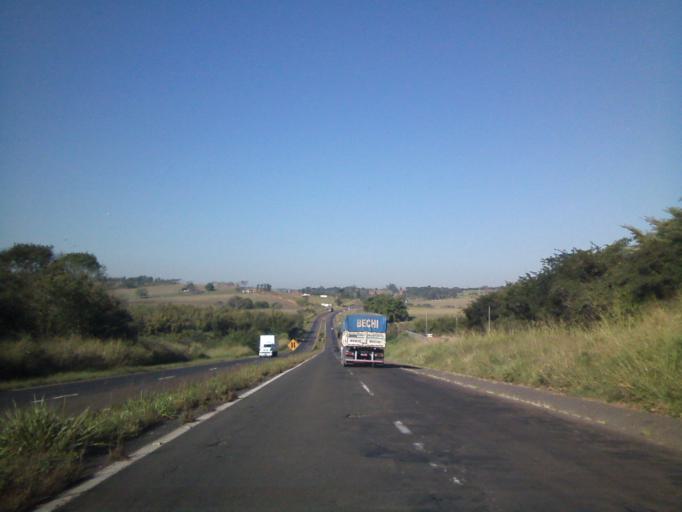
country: BR
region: Sao Paulo
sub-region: Presidente Prudente
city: Presidente Prudente
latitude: -22.2017
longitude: -51.4342
